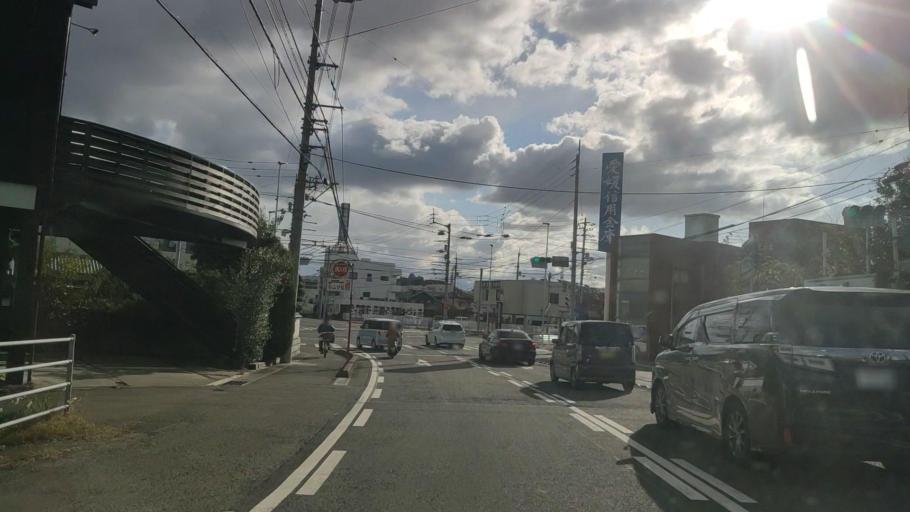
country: JP
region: Ehime
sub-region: Shikoku-chuo Shi
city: Matsuyama
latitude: 33.8559
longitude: 132.7429
